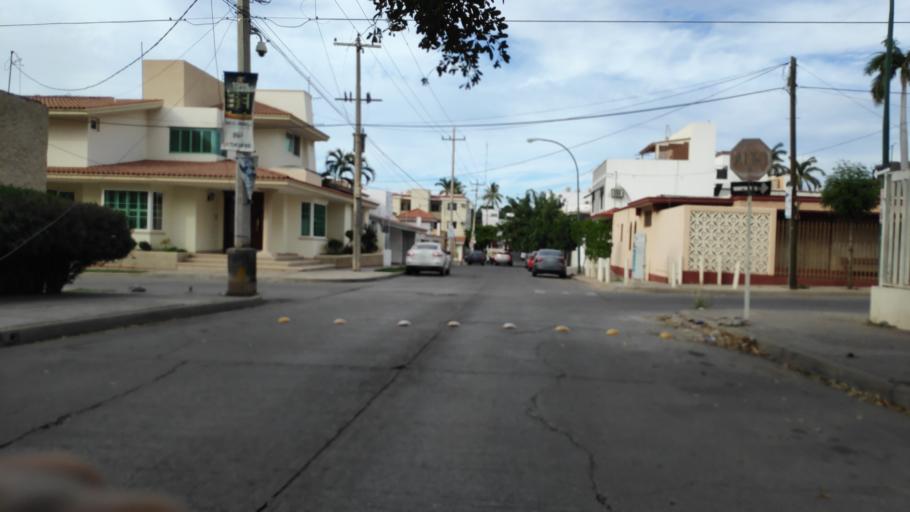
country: MX
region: Sinaloa
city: Culiacan
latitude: 24.7926
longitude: -107.3962
